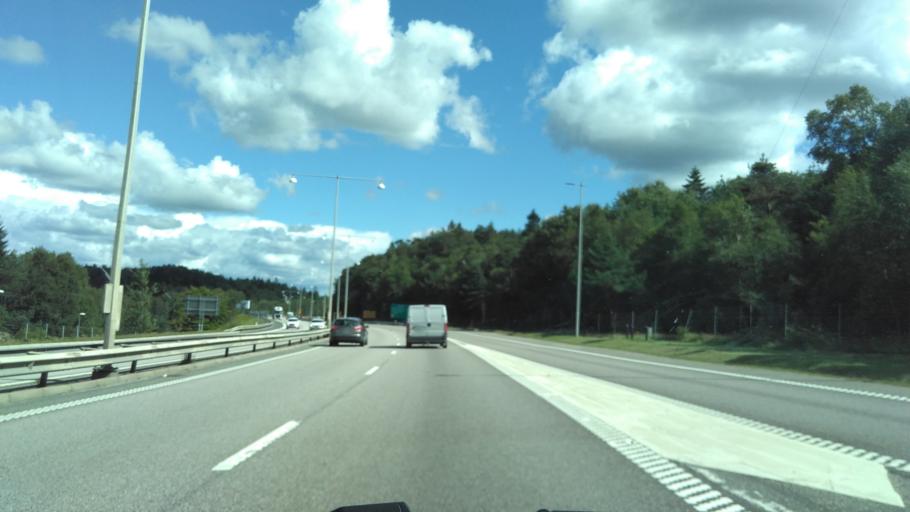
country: SE
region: Vaestra Goetaland
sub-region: Molndal
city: Moelndal
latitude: 57.6757
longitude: 12.0319
